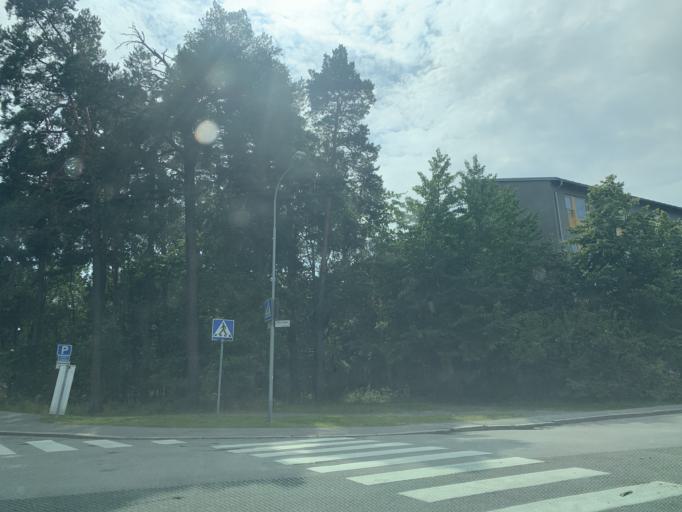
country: SE
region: Stockholm
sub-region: Norrtalje Kommun
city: Bergshamra
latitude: 59.3828
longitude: 18.0291
